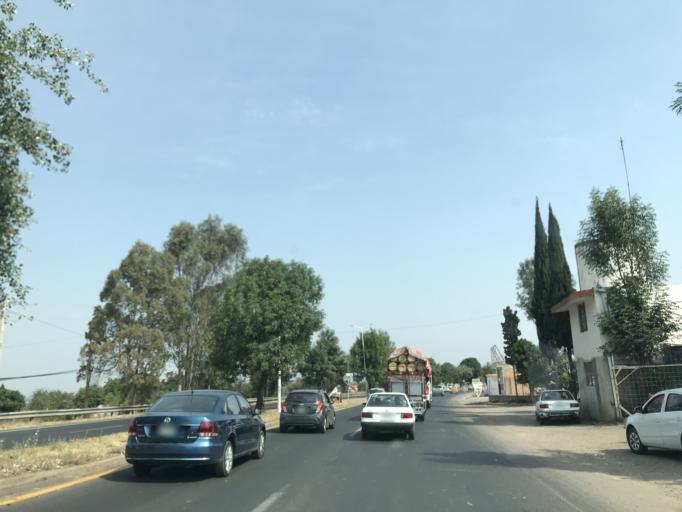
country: MX
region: Tlaxcala
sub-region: Teolocholco
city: Teolocholco
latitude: 19.2554
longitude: -98.1995
